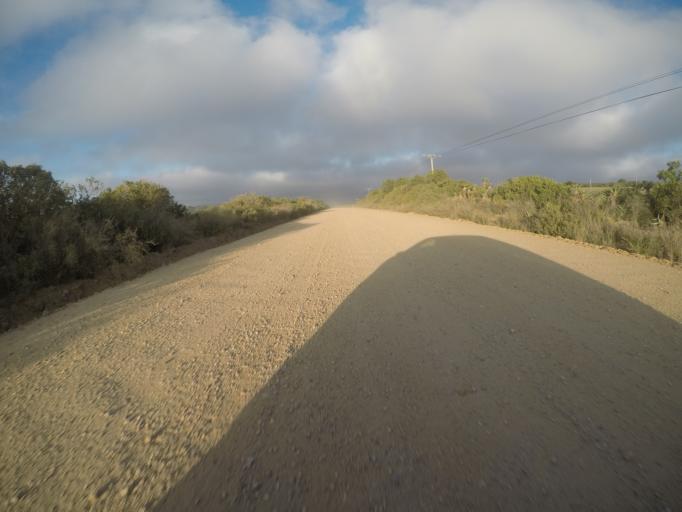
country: ZA
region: Western Cape
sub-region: Eden District Municipality
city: Mossel Bay
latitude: -34.1106
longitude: 22.0561
